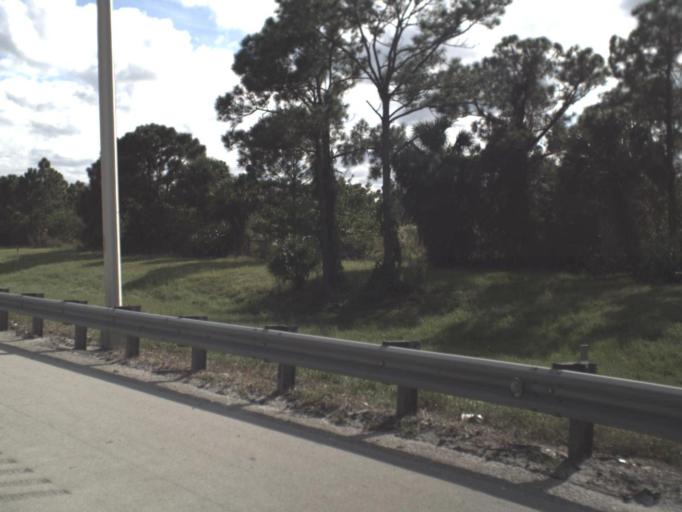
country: US
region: Florida
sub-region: Martin County
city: North River Shores
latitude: 27.2040
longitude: -80.3311
